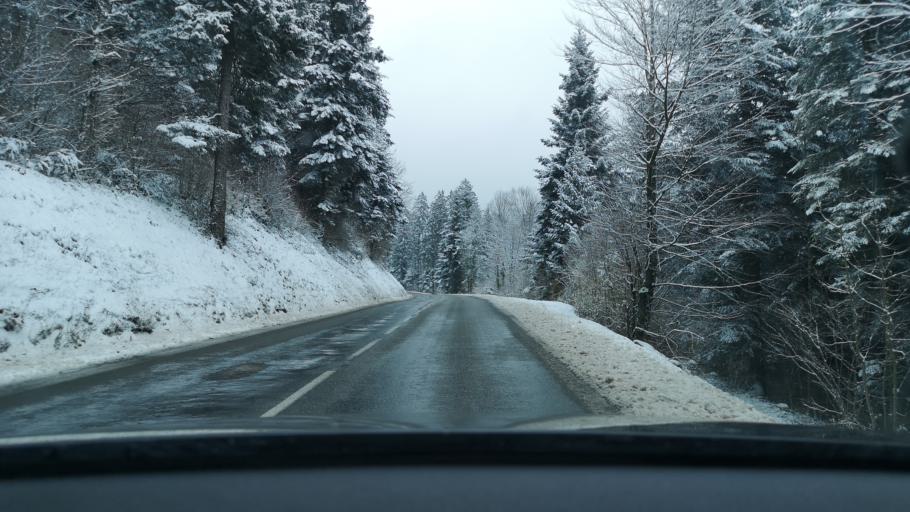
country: FR
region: Rhone-Alpes
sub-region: Departement de l'Ain
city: Oyonnax
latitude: 46.2528
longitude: 5.6796
